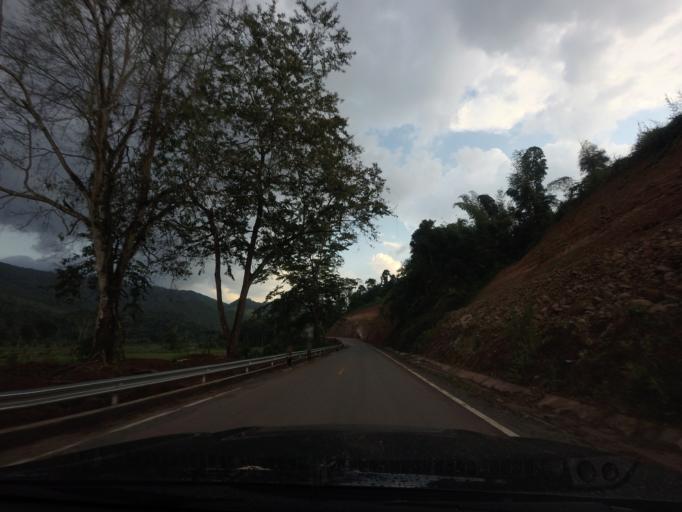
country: TH
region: Nan
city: Bo Kluea
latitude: 19.2194
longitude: 101.1834
